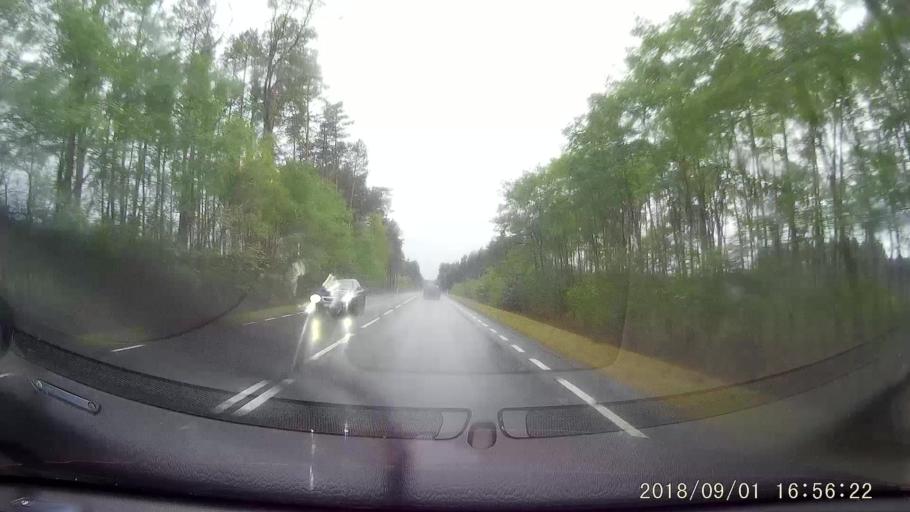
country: PL
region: Lubusz
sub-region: Powiat zielonogorski
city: Czerwiensk
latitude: 51.9430
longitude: 15.4355
